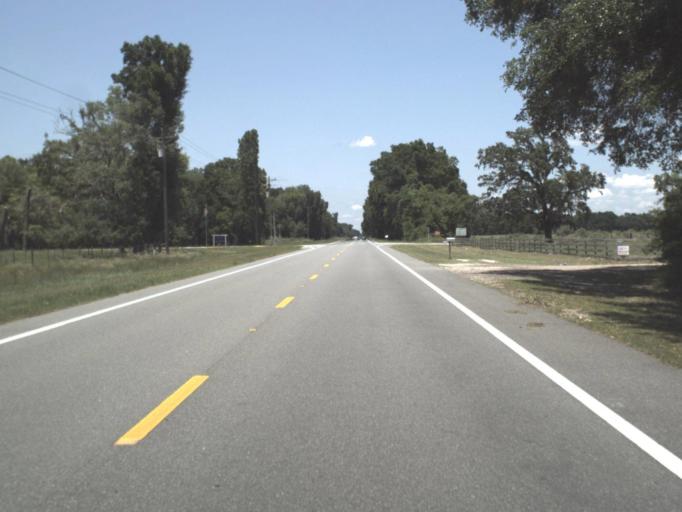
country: US
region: Florida
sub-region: Dixie County
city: Cross City
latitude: 29.7654
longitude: -82.9806
